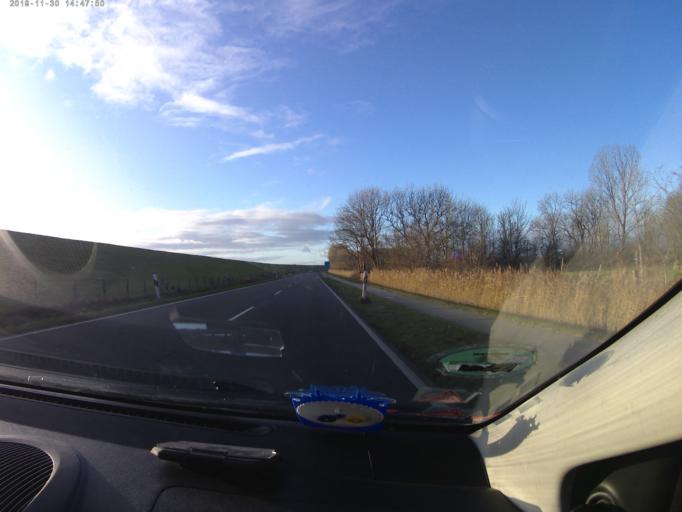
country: DE
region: Lower Saxony
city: Leer
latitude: 53.2338
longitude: 7.4169
